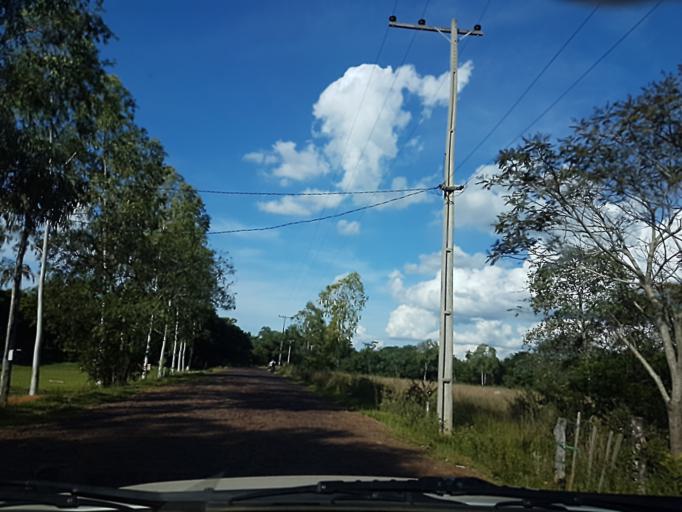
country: PY
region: Cordillera
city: Arroyos y Esteros
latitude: -24.9977
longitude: -57.1718
